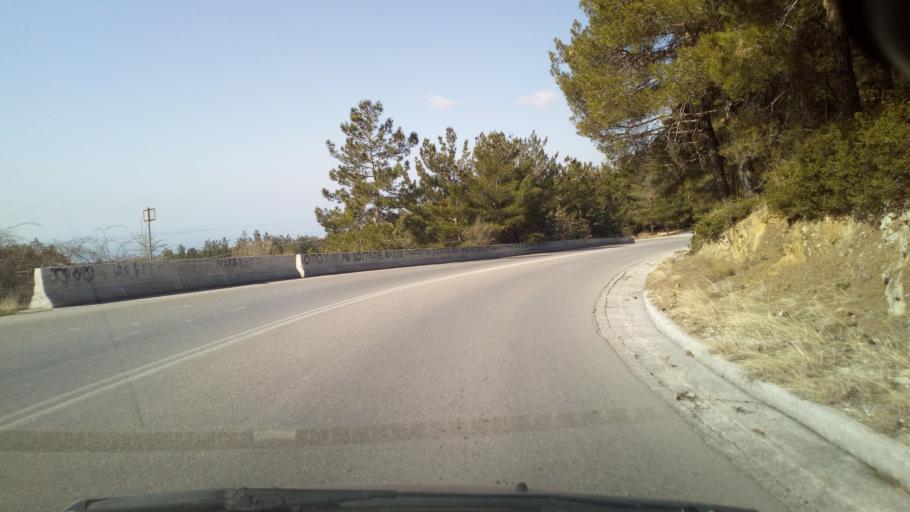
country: GR
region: Central Macedonia
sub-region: Nomos Thessalonikis
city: Panorama
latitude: 40.6119
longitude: 23.0576
